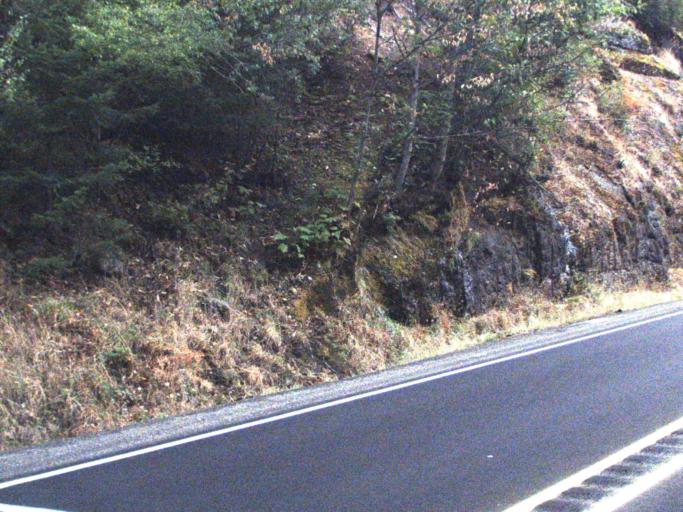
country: US
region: Washington
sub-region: Pierce County
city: Buckley
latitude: 46.6784
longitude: -121.5308
